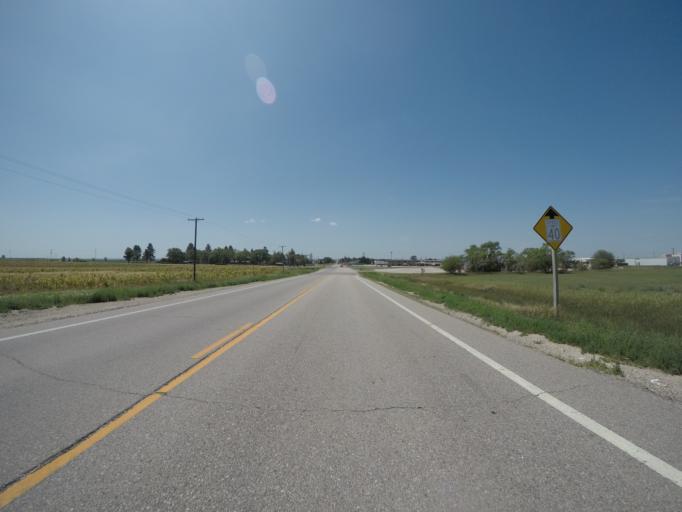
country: US
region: Kansas
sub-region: Osborne County
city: Osborne
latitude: 39.4548
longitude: -98.6947
